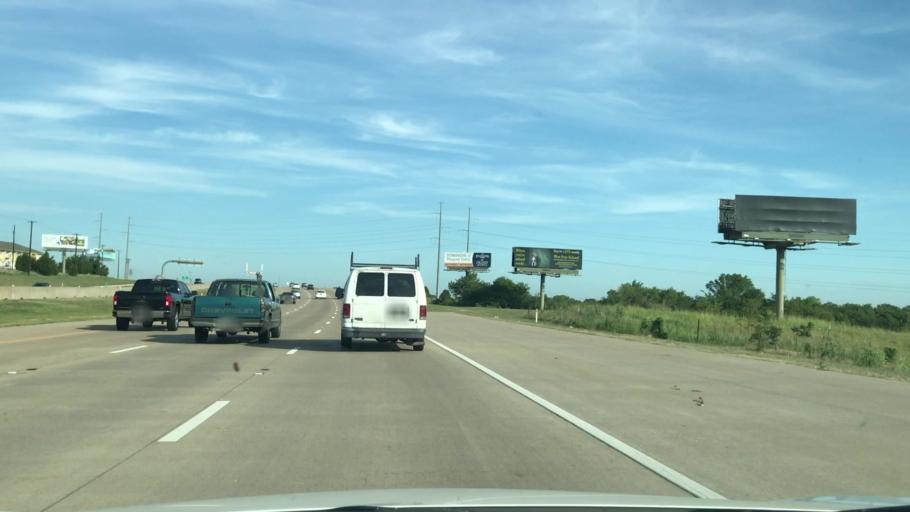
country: US
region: Texas
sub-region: Dallas County
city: Rowlett
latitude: 32.9463
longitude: -96.5605
